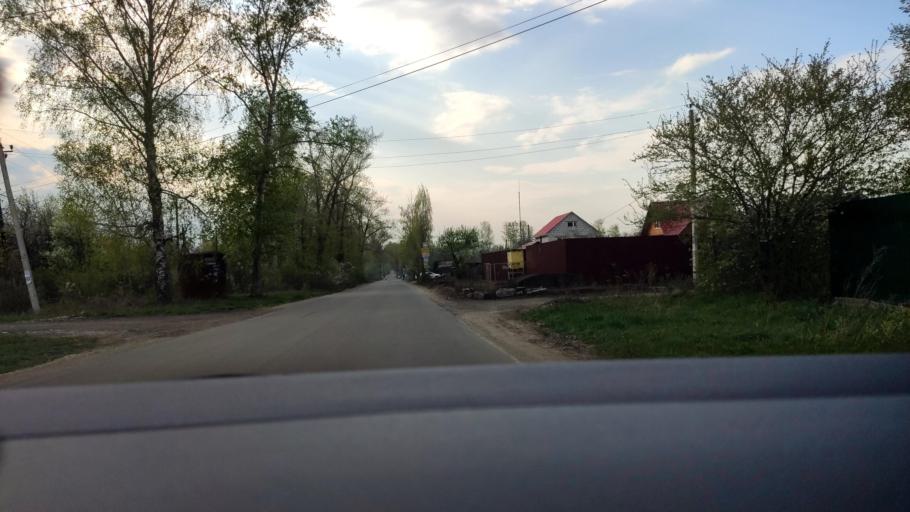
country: RU
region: Voronezj
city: Voronezh
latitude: 51.5998
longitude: 39.1660
